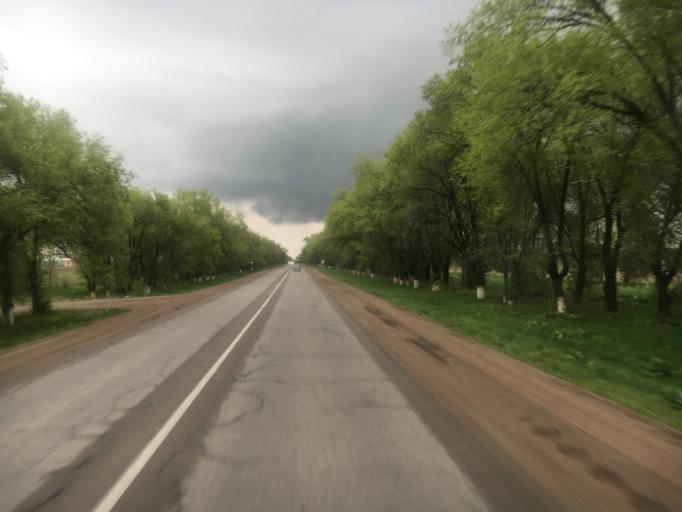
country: KZ
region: Almaty Oblysy
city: Burunday
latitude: 43.2526
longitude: 76.6681
